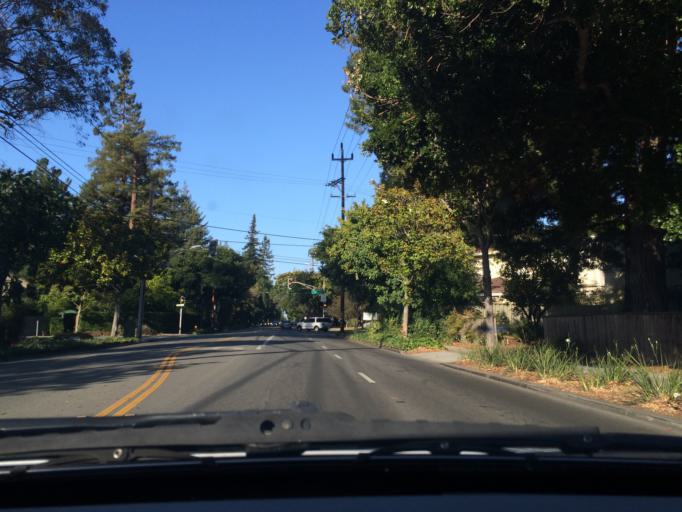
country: US
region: California
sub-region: Santa Clara County
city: Palo Alto
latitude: 37.4401
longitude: -122.1503
